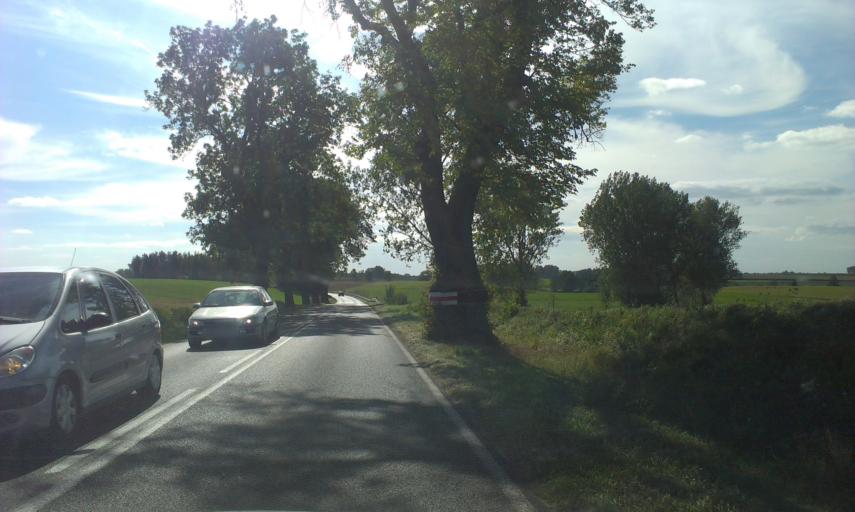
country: PL
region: Greater Poland Voivodeship
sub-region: Powiat pilski
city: Lobzenica
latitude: 53.2219
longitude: 17.2379
